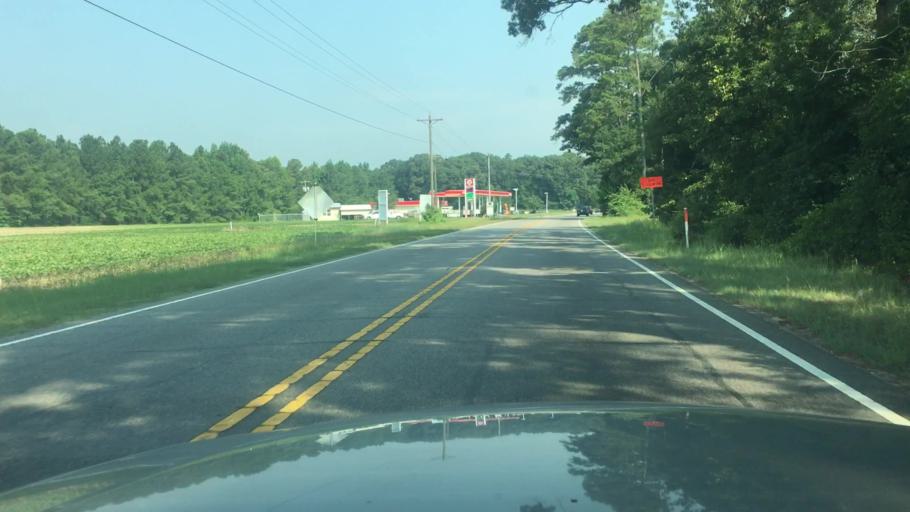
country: US
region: North Carolina
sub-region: Cumberland County
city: Hope Mills
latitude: 34.9337
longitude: -78.9191
